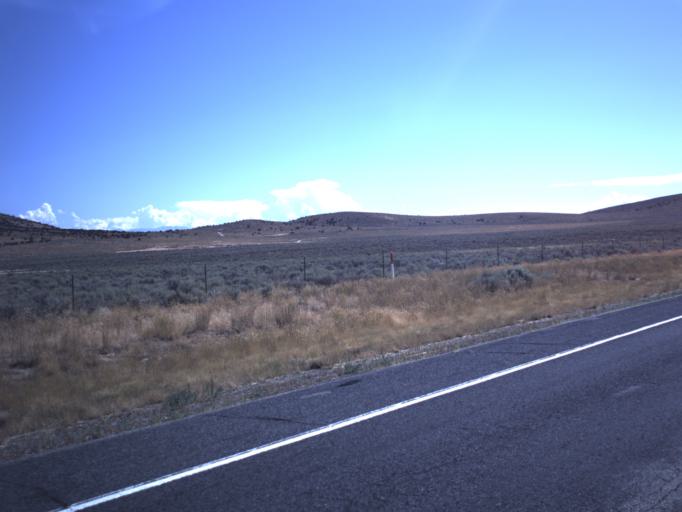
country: US
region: Utah
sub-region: Utah County
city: Eagle Mountain
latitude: 40.0777
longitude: -112.3941
